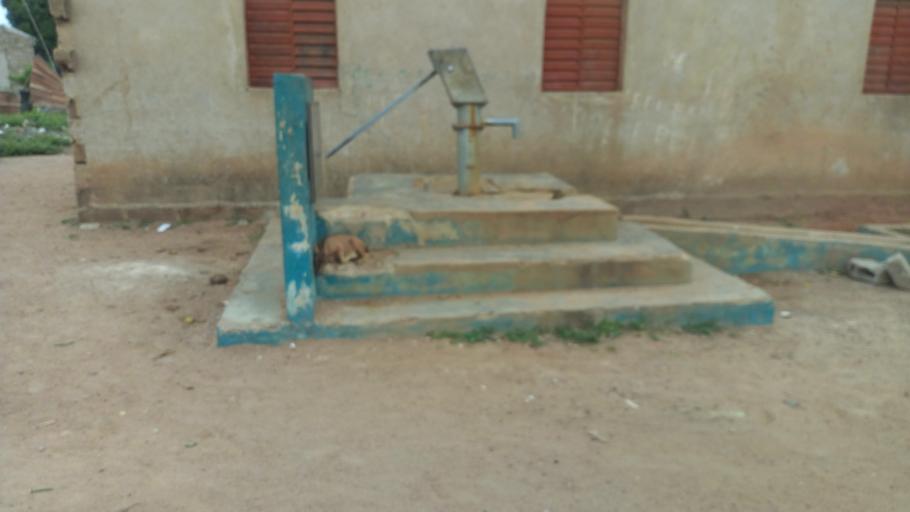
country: CI
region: Vallee du Bandama
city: Bouake
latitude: 7.7292
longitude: -5.0437
